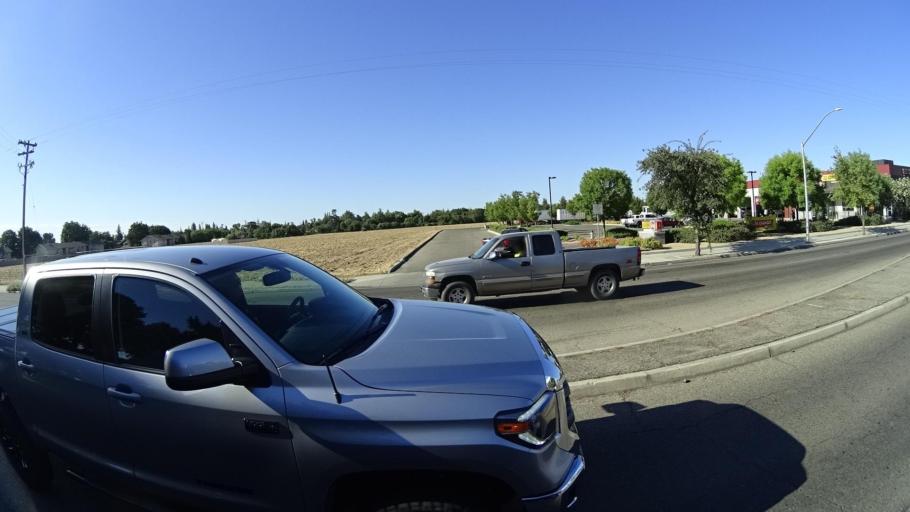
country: US
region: California
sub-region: Fresno County
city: Sunnyside
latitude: 36.7362
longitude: -119.6942
